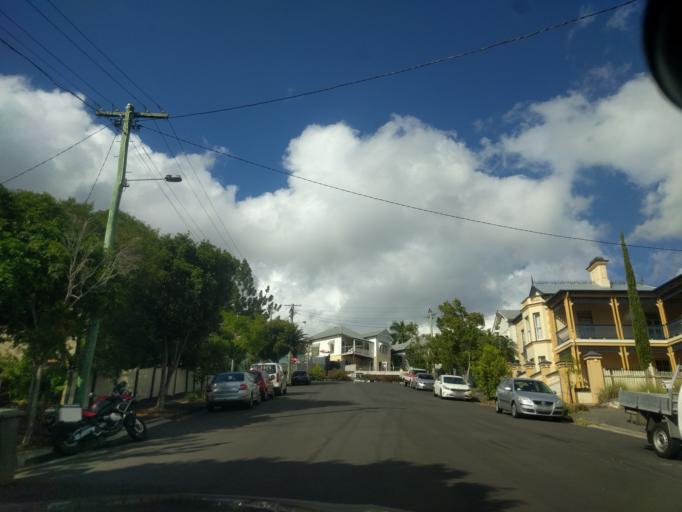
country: AU
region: Queensland
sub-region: Brisbane
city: Balmoral
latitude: -27.4612
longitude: 153.0476
